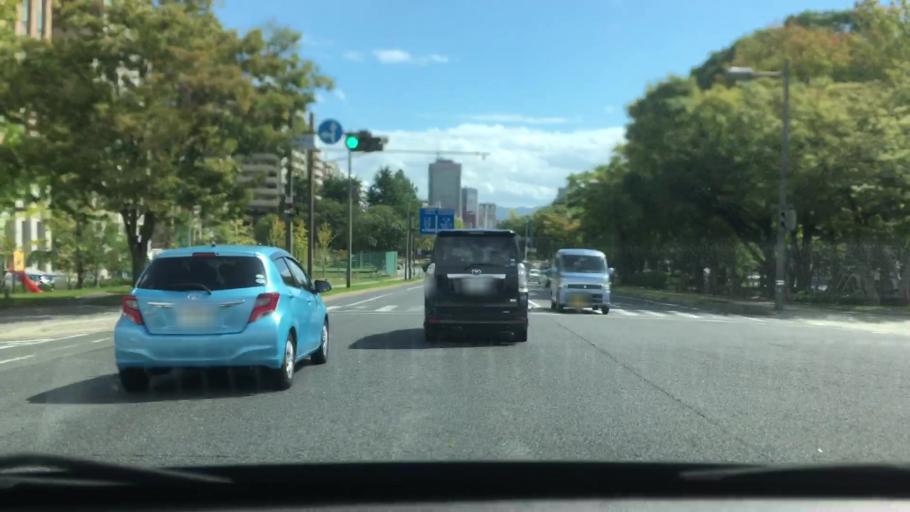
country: JP
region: Hiroshima
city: Hiroshima-shi
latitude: 34.3926
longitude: 132.4438
